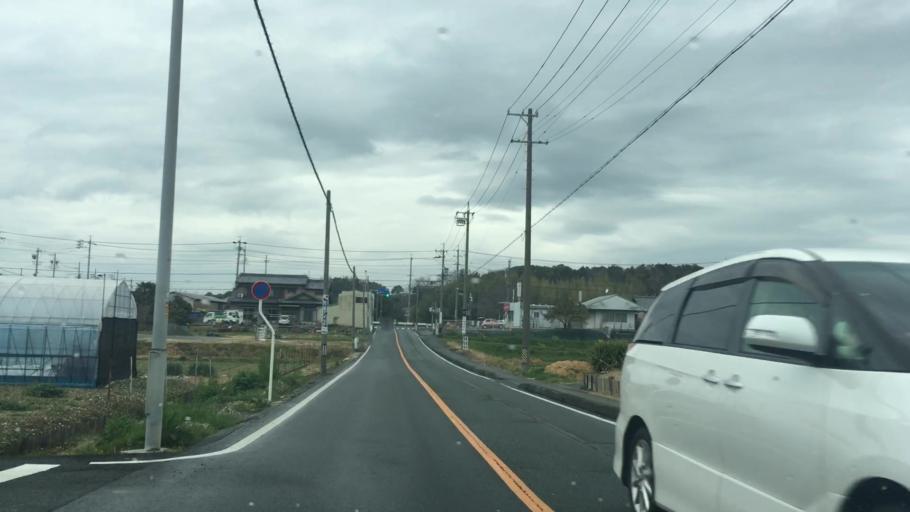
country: JP
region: Aichi
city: Toyohashi
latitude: 34.7221
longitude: 137.4179
